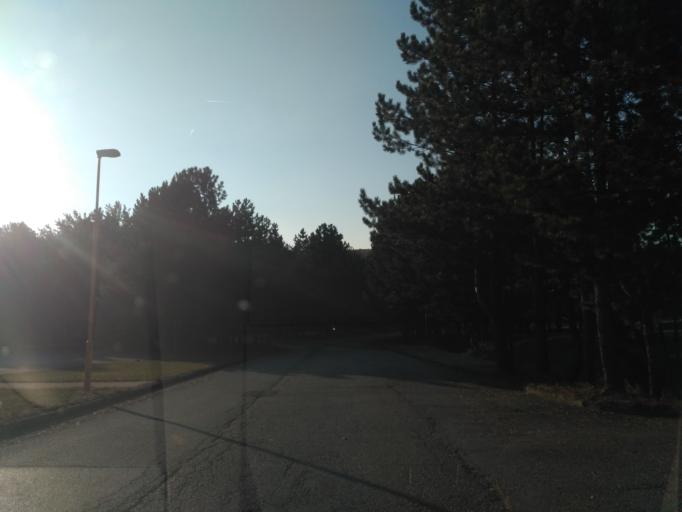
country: SK
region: Kosicky
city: Kosice
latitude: 48.7726
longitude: 21.2899
